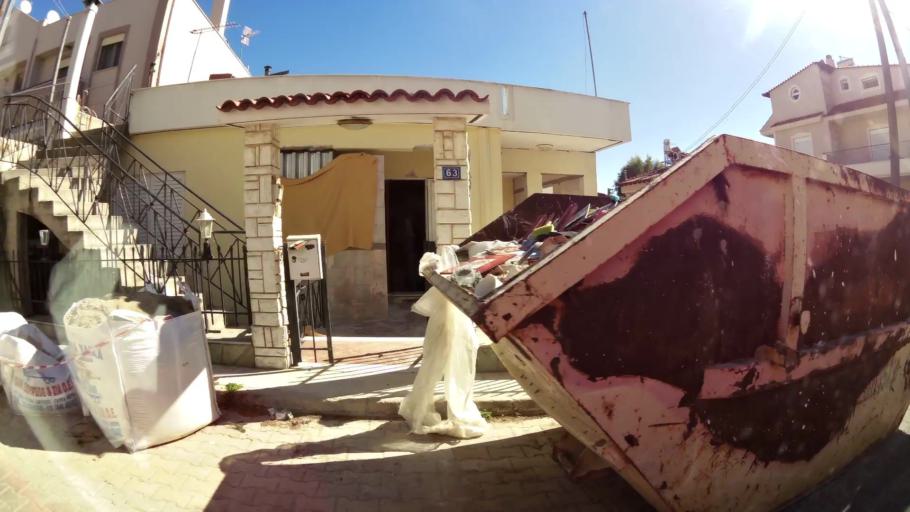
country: GR
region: Attica
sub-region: Nomarchia Anatolikis Attikis
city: Leondarion
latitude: 38.0025
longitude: 23.8511
